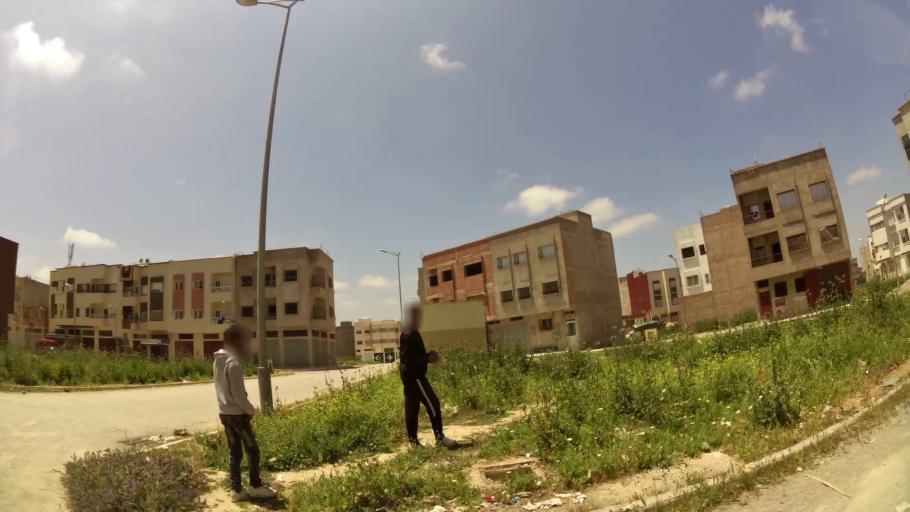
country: MA
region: Fes-Boulemane
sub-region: Fes
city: Fes
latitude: 34.0355
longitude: -5.0548
